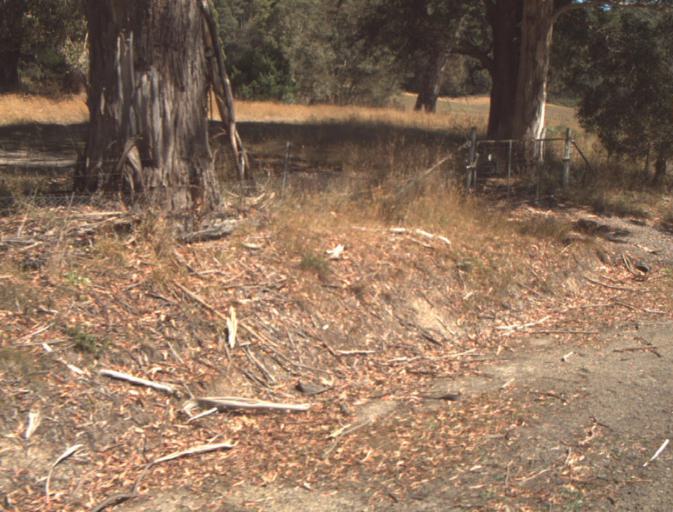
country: AU
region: Tasmania
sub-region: Dorset
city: Scottsdale
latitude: -41.3105
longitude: 147.3919
